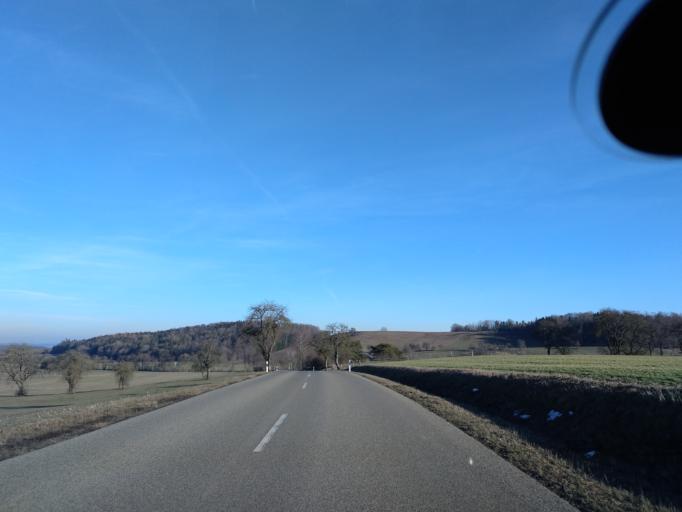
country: DE
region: Baden-Wuerttemberg
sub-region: Regierungsbezirk Stuttgart
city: Obersontheim
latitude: 49.0864
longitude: 9.9522
